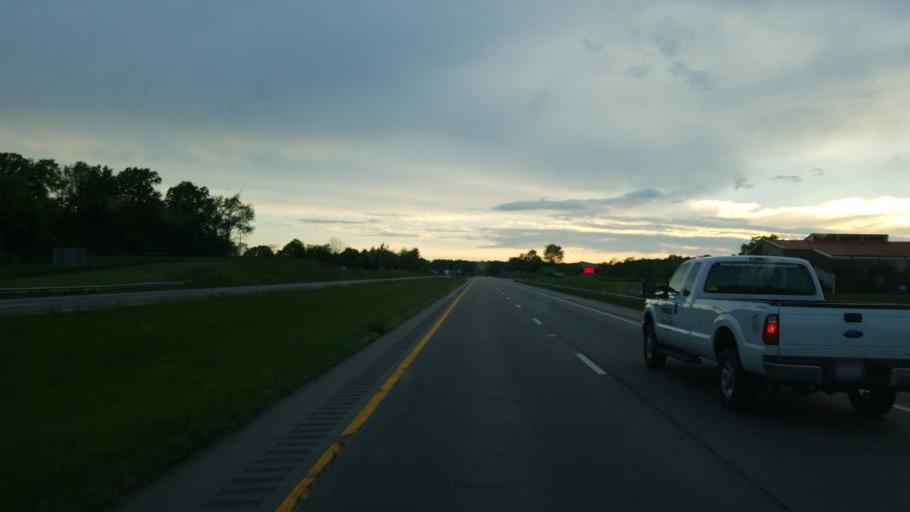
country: US
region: Ohio
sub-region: Wayne County
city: Wooster
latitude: 40.7930
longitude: -81.9792
